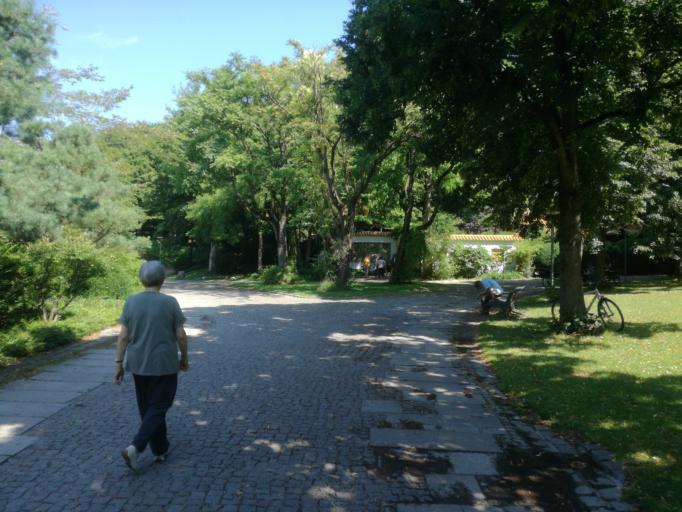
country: DE
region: Bavaria
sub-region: Upper Bavaria
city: Neuried
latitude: 48.1228
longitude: 11.5135
